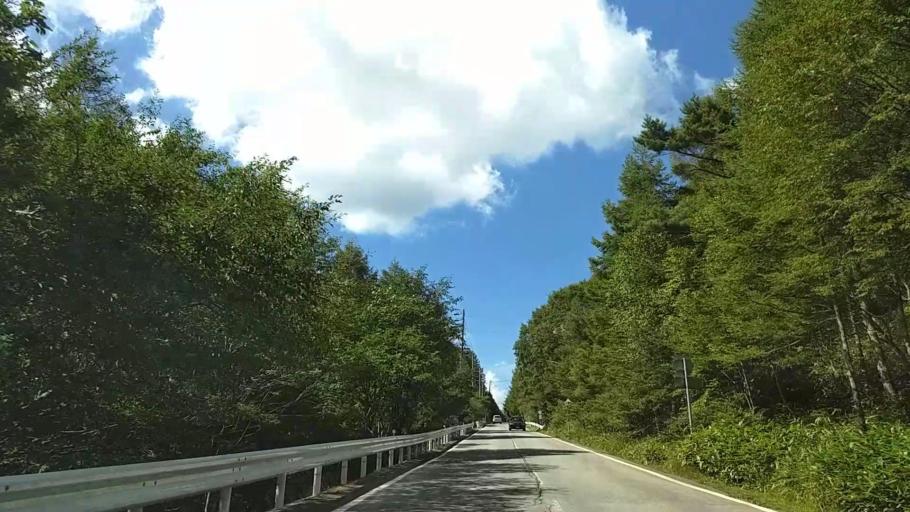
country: JP
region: Nagano
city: Chino
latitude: 36.0836
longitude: 138.2814
